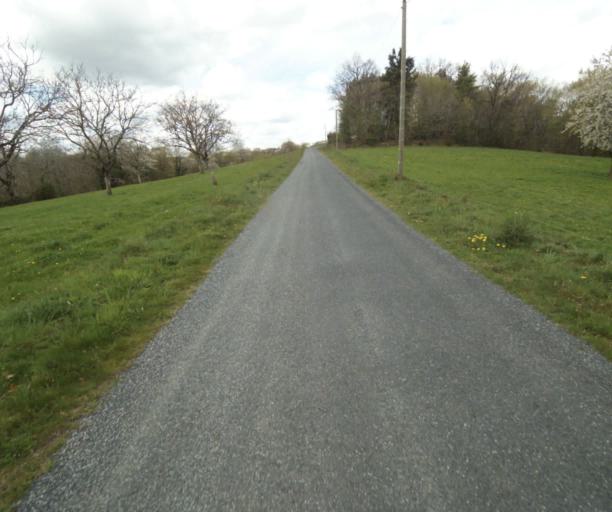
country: FR
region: Limousin
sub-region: Departement de la Correze
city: Sainte-Fortunade
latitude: 45.1935
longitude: 1.8606
